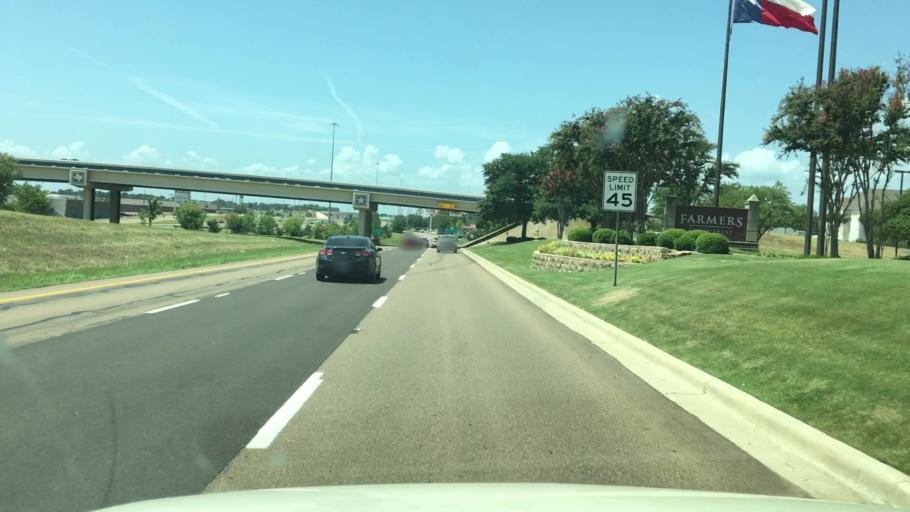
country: US
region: Arkansas
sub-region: Miller County
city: Texarkana
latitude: 33.4618
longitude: -94.0763
